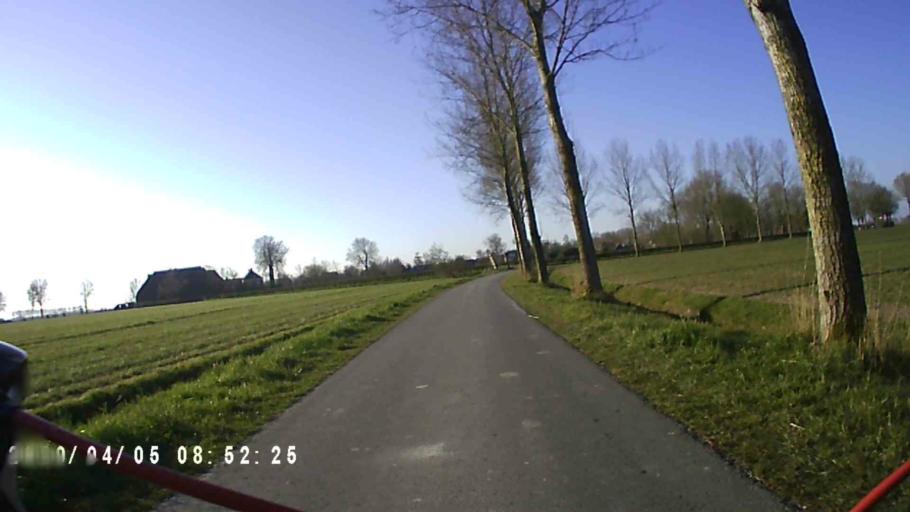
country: NL
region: Groningen
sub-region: Gemeente Zuidhorn
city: Aduard
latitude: 53.3105
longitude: 6.4656
